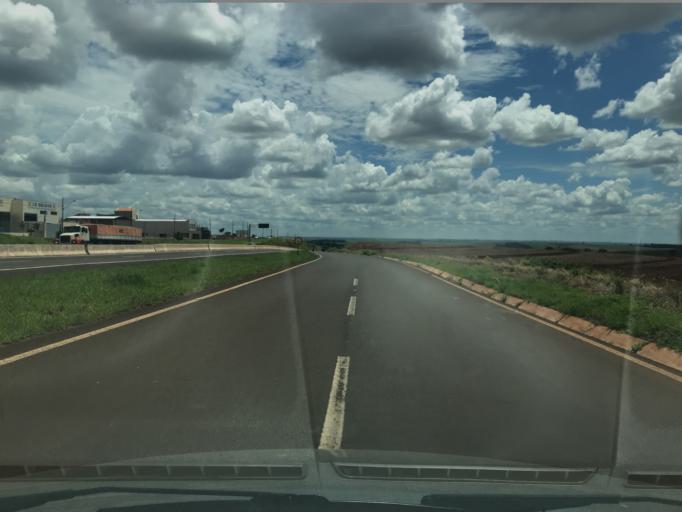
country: BR
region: Parana
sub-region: Maringa
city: Maringa
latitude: -23.3781
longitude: -51.9153
